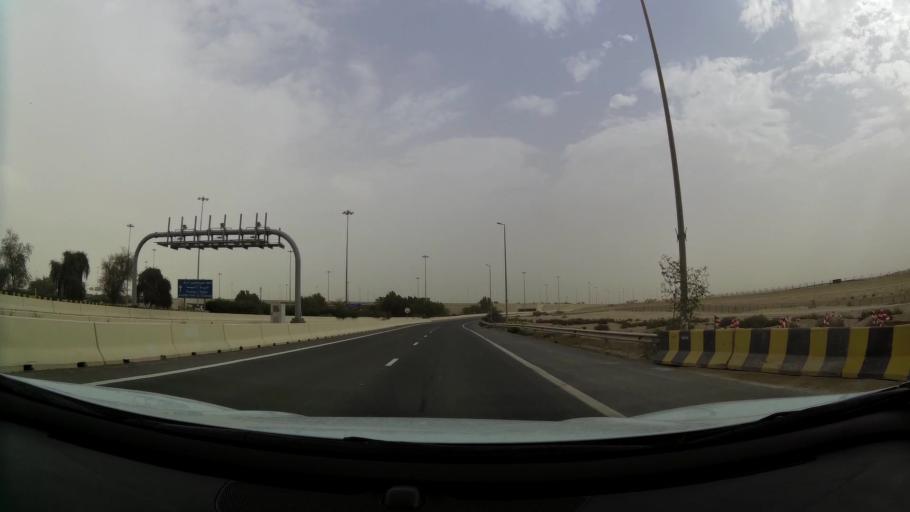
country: AE
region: Abu Dhabi
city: Abu Dhabi
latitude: 24.4797
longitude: 54.6406
